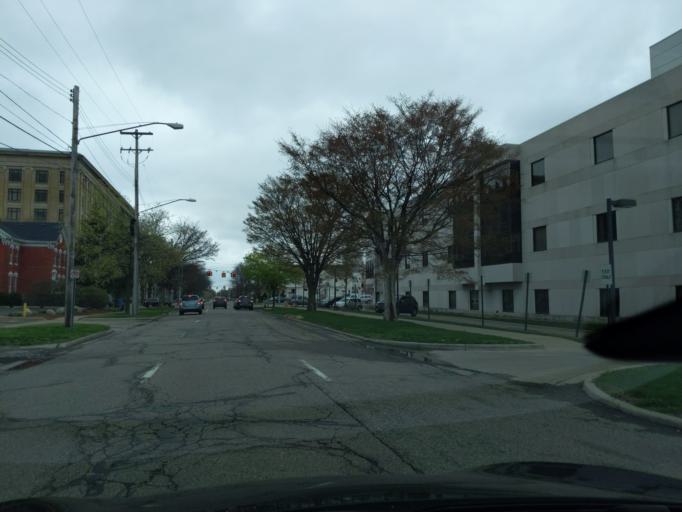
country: US
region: Michigan
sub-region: Ingham County
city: Lansing
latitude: 42.7291
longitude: -84.5570
